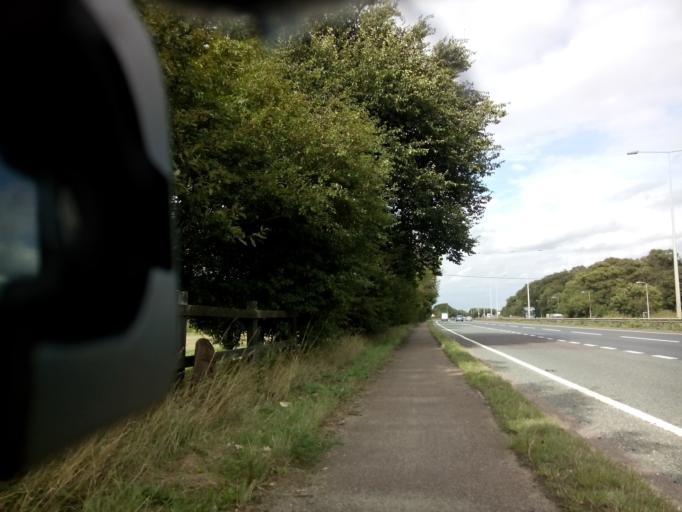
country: GB
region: England
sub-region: Suffolk
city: Capel Saint Mary
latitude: 52.0084
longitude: 1.0617
